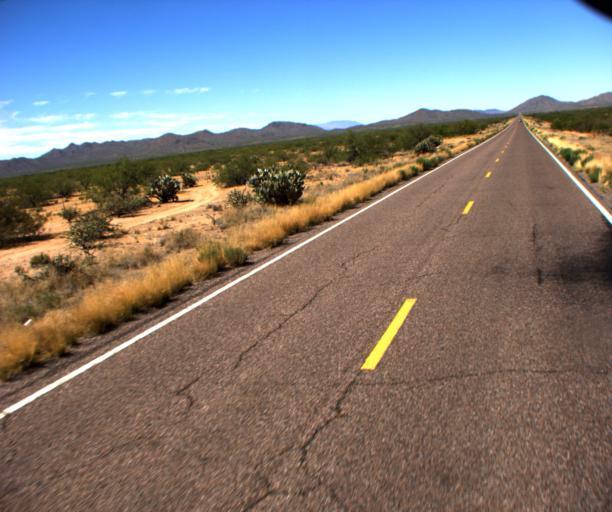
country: US
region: Arizona
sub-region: Yavapai County
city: Congress
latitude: 34.1362
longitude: -112.9183
